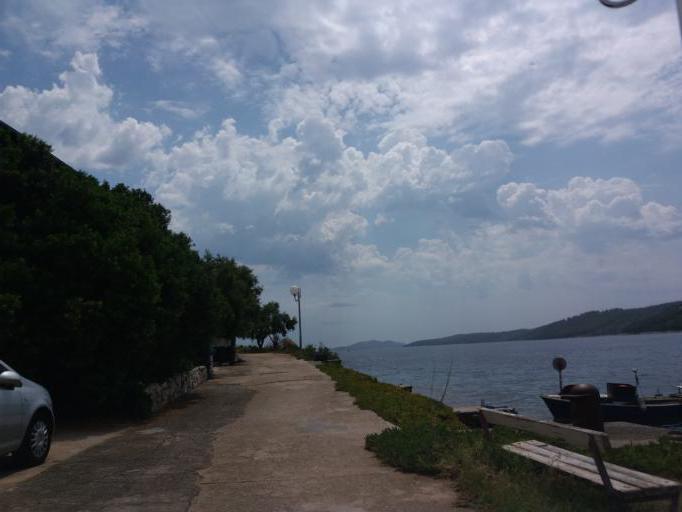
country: HR
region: Zadarska
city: Sali
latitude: 43.9369
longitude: 15.1683
